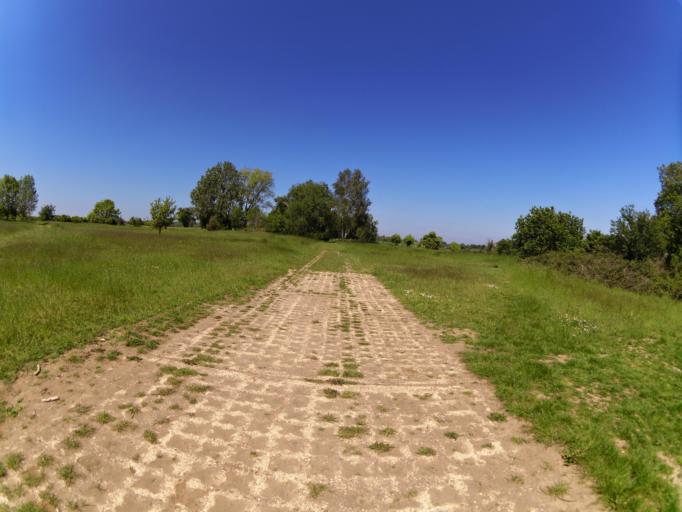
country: GB
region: England
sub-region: Essex
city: Mistley
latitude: 51.9798
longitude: 1.1461
